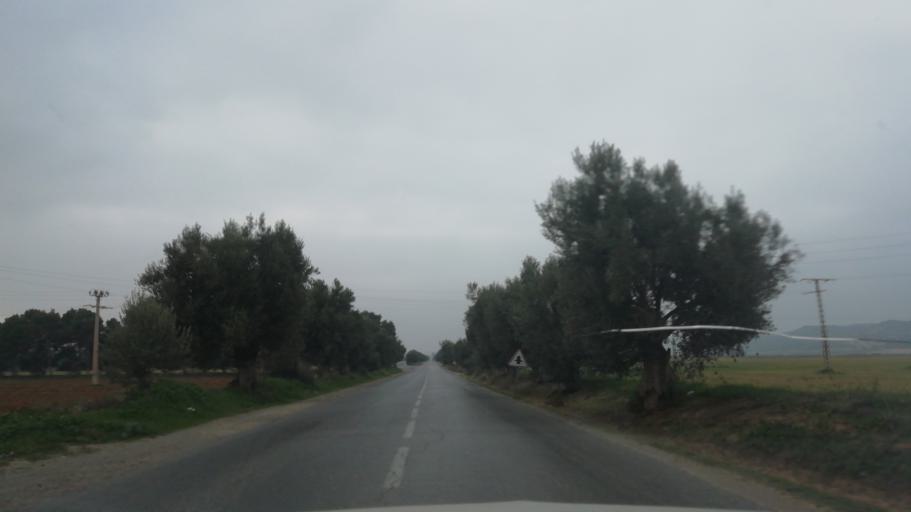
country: DZ
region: Sidi Bel Abbes
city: Sfizef
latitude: 35.2277
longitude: -0.2677
